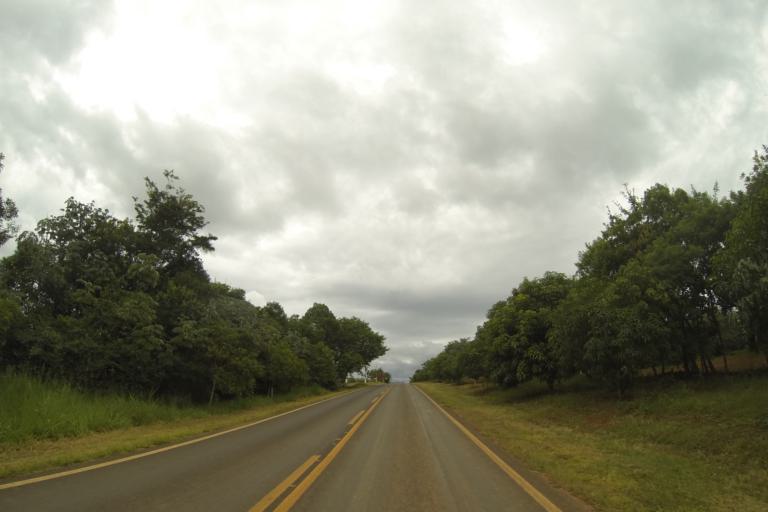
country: BR
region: Minas Gerais
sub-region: Bambui
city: Bambui
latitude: -20.0054
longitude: -46.2073
